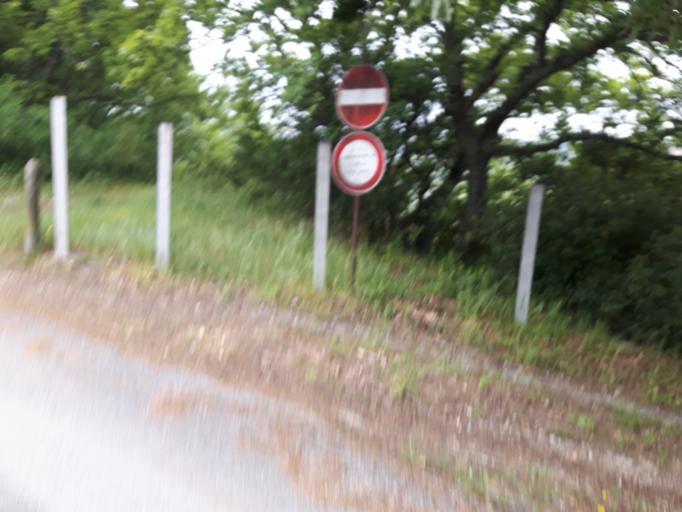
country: IT
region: Abruzzo
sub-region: Provincia di Chieti
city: Vasto
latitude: 42.1406
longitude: 14.6946
